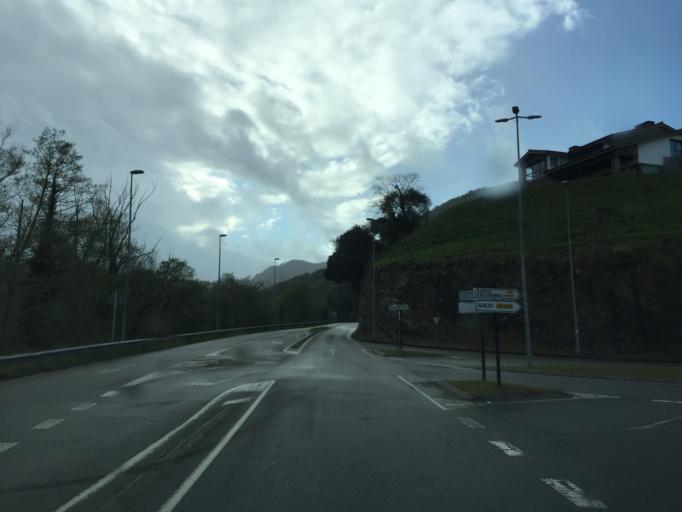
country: ES
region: Cantabria
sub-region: Provincia de Cantabria
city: Tresviso
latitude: 43.3266
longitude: -4.5862
